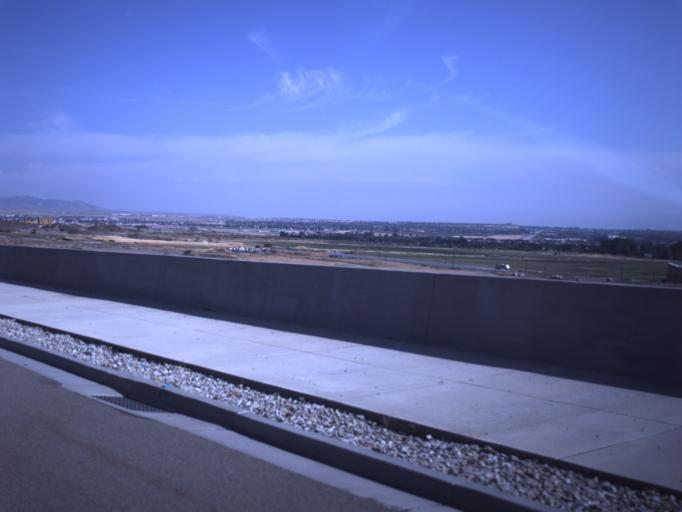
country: US
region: Utah
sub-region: Salt Lake County
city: Bluffdale
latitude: 40.4791
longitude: -111.9826
